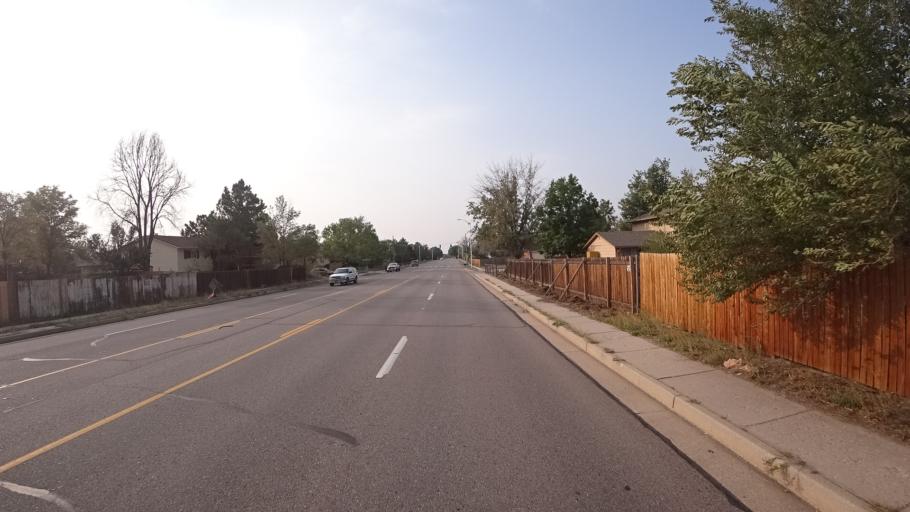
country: US
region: Colorado
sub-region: El Paso County
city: Stratmoor
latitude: 38.8015
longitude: -104.7435
